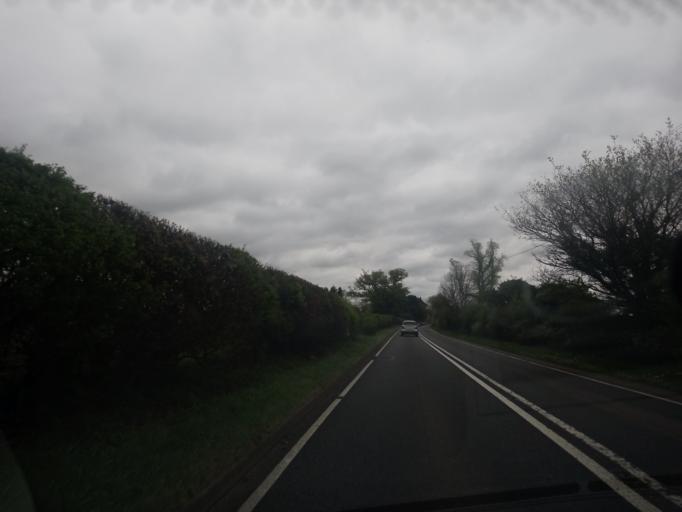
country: GB
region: England
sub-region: Telford and Wrekin
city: Chetwynd
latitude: 52.8054
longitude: -2.4332
